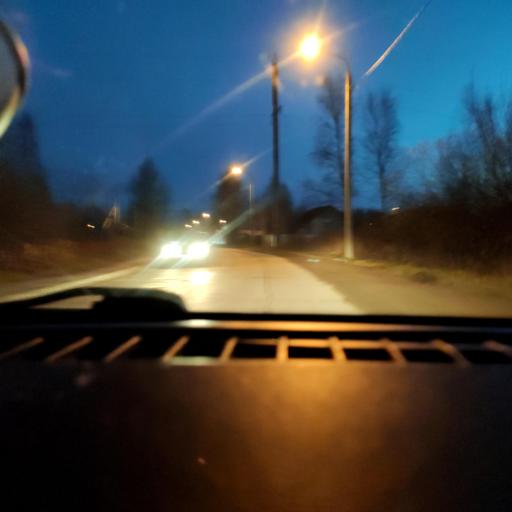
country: RU
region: Perm
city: Kondratovo
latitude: 58.0247
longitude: 56.1678
